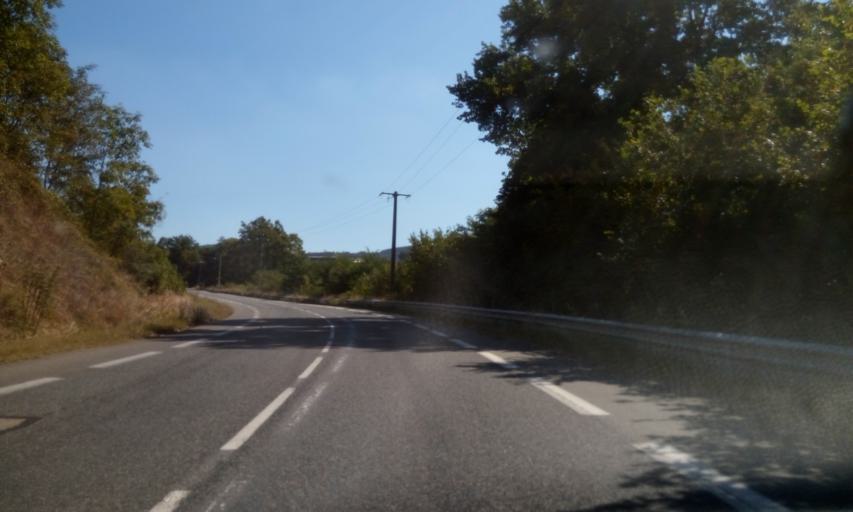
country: FR
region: Rhone-Alpes
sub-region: Departement du Rhone
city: Amplepuis
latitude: 45.9718
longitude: 4.3538
